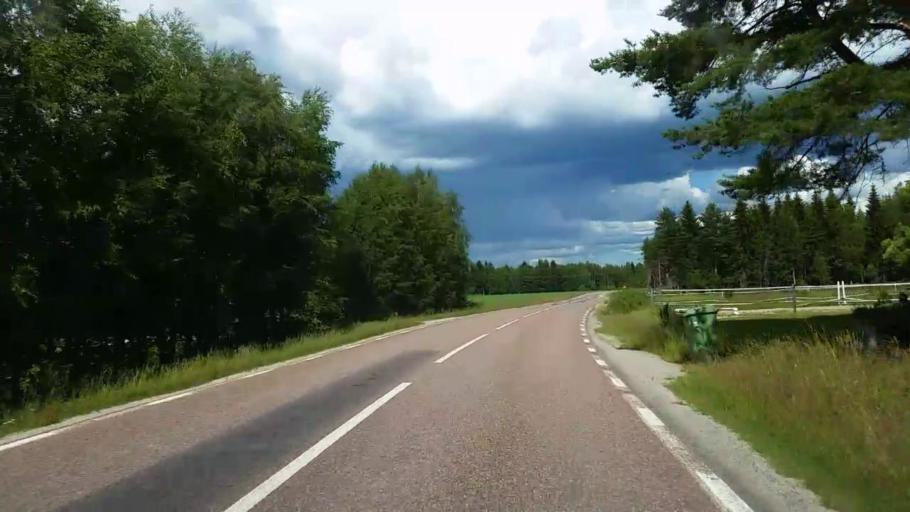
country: SE
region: Gaevleborg
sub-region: Ovanakers Kommun
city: Edsbyn
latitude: 61.3386
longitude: 15.5424
